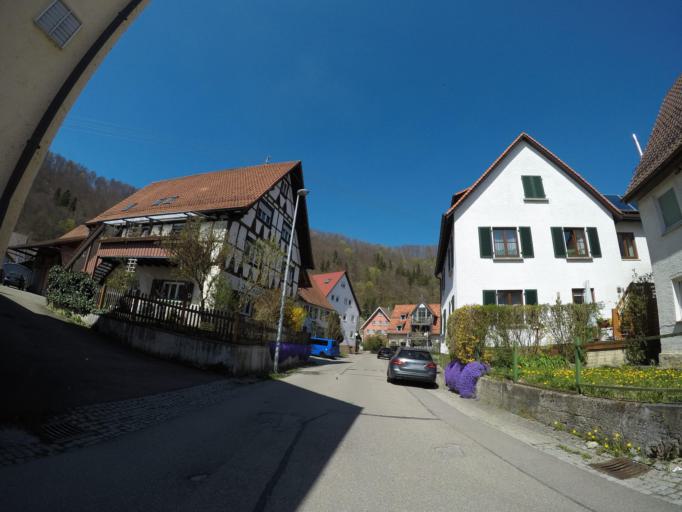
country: DE
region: Baden-Wuerttemberg
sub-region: Tuebingen Region
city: Blaubeuren
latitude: 48.4030
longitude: 9.7667
